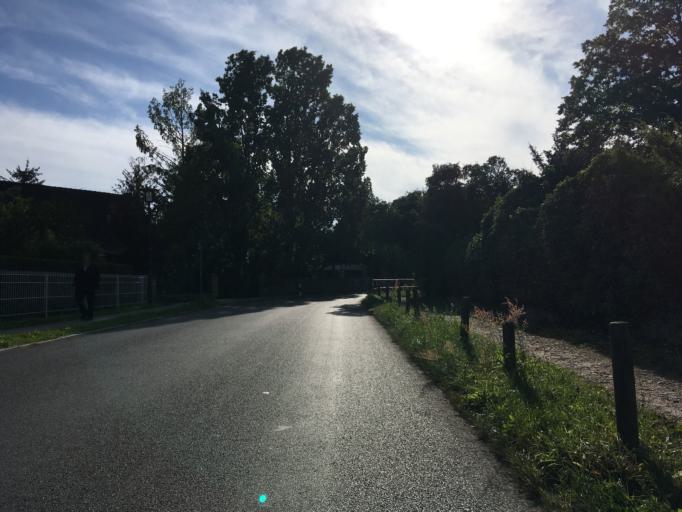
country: DE
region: Brandenburg
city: Hoppegarten
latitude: 52.5170
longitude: 13.6508
